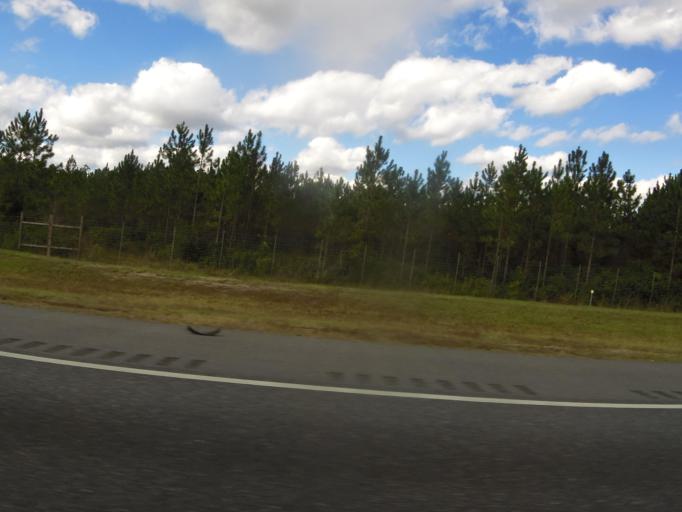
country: US
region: Florida
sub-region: Bradford County
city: Starke
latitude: 29.9906
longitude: -82.0999
